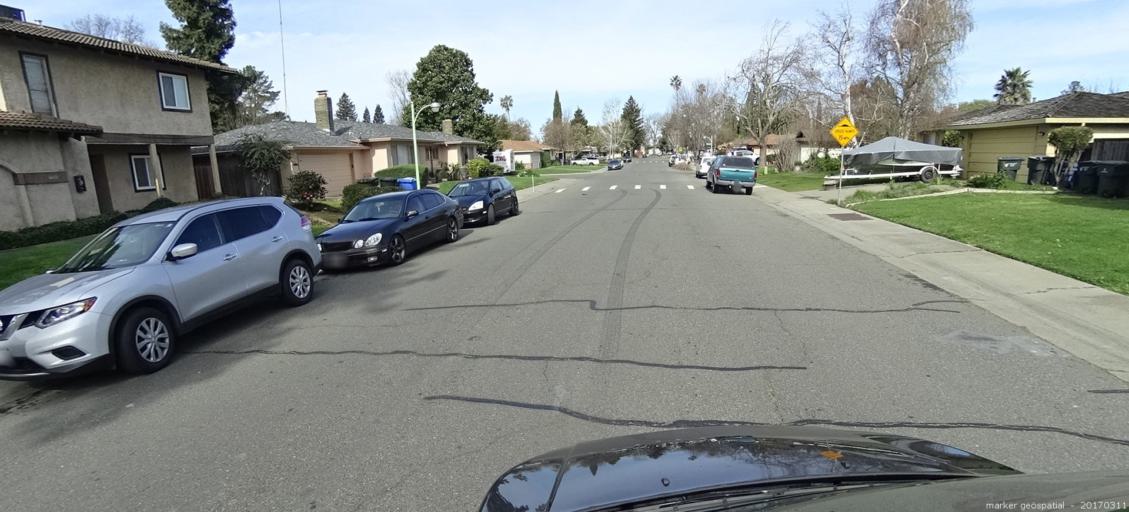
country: US
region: California
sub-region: Yolo County
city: West Sacramento
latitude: 38.5068
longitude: -121.5510
